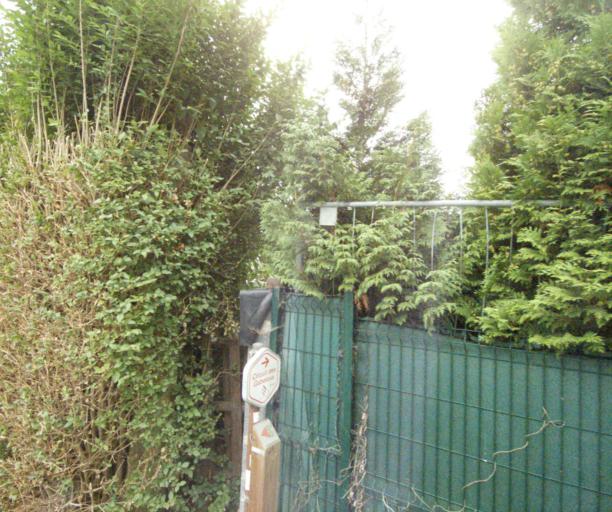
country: FR
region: Nord-Pas-de-Calais
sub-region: Departement du Nord
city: Neuville-en-Ferrain
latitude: 50.7699
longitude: 3.1636
